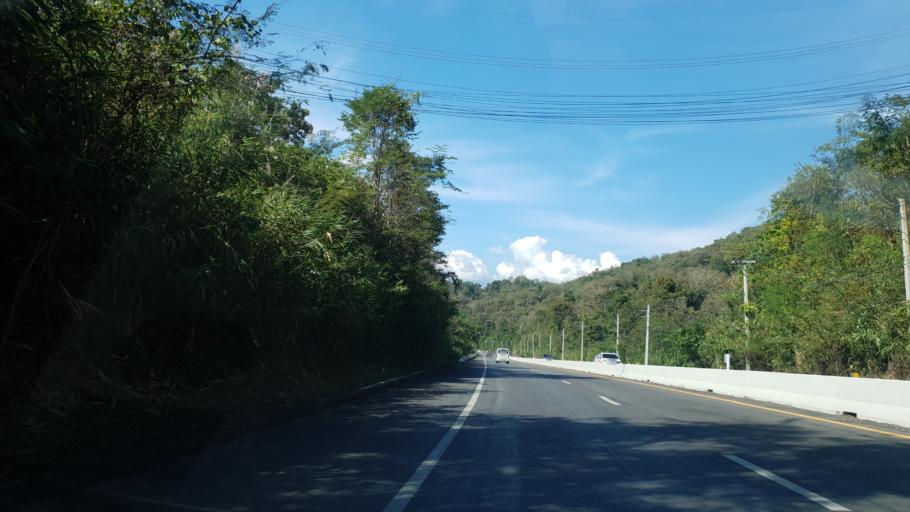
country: TH
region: Phrae
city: Den Chai
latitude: 17.8578
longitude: 100.0462
